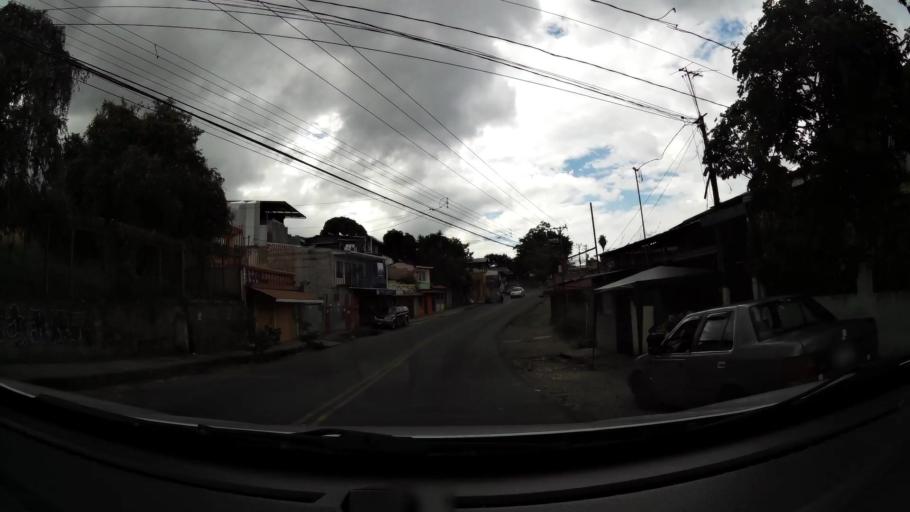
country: CR
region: San Jose
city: San Felipe
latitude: 9.9034
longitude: -84.1047
